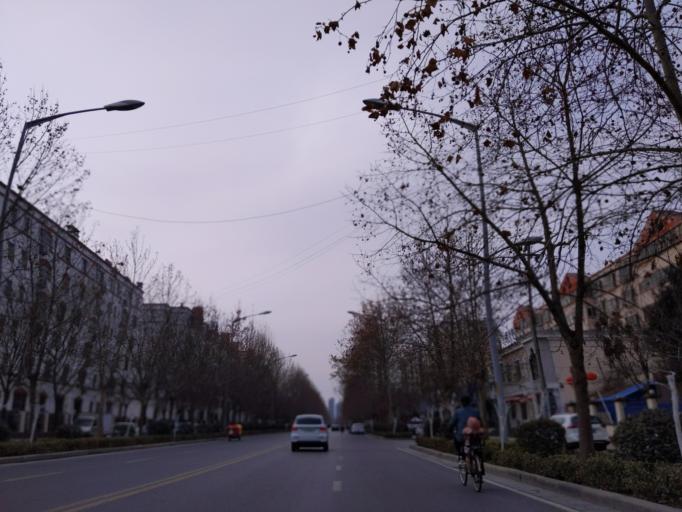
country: CN
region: Henan Sheng
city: Zhongyuanlu
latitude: 35.7571
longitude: 115.0533
